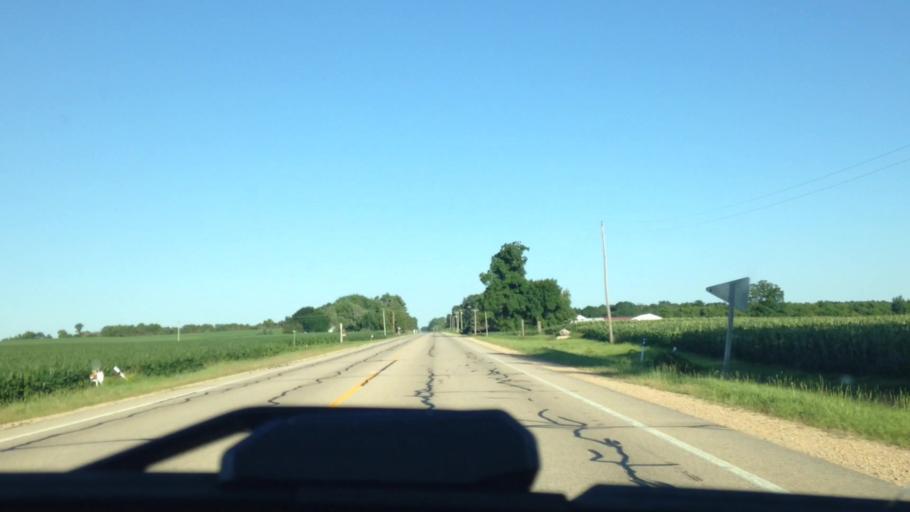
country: US
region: Wisconsin
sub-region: Dane County
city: De Forest
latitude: 43.3328
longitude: -89.2659
